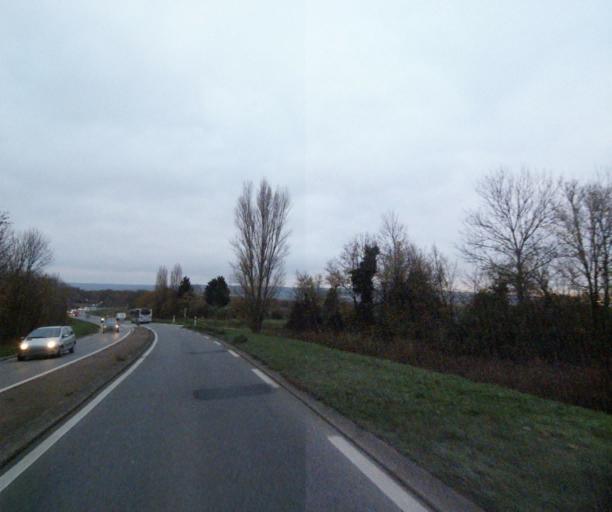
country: FR
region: Ile-de-France
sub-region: Departement des Yvelines
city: Medan
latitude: 48.9547
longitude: 1.9804
